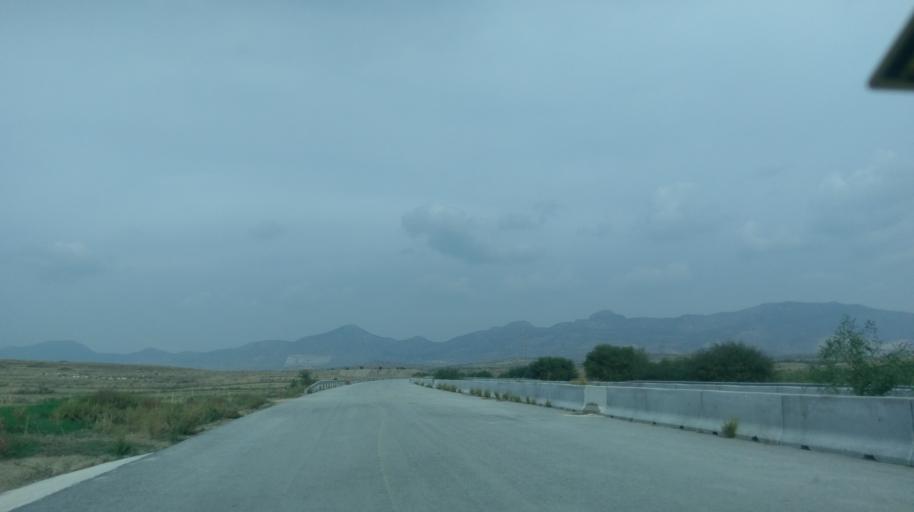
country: CY
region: Lefkosia
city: Nicosia
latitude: 35.2227
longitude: 33.4011
